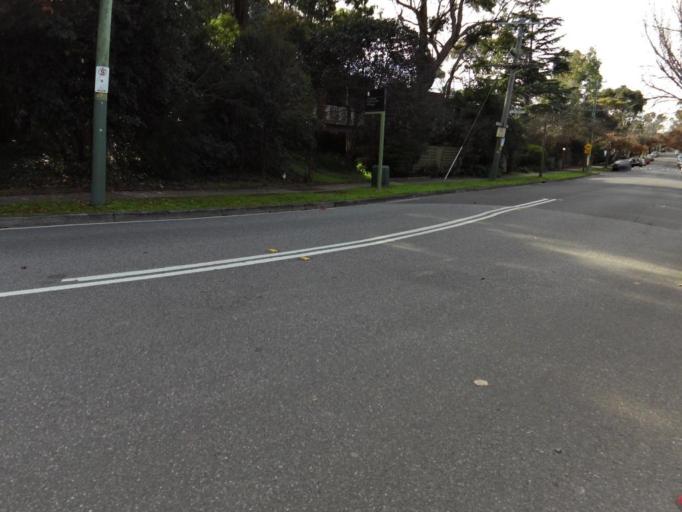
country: AU
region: Victoria
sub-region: Whitehorse
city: Blackburn
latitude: -37.8207
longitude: 145.1414
